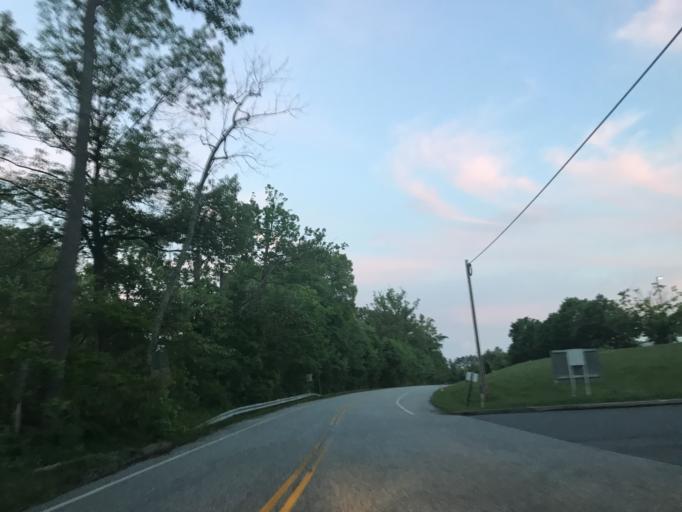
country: US
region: Maryland
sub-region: Harford County
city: Joppatowne
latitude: 39.4487
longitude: -76.3211
